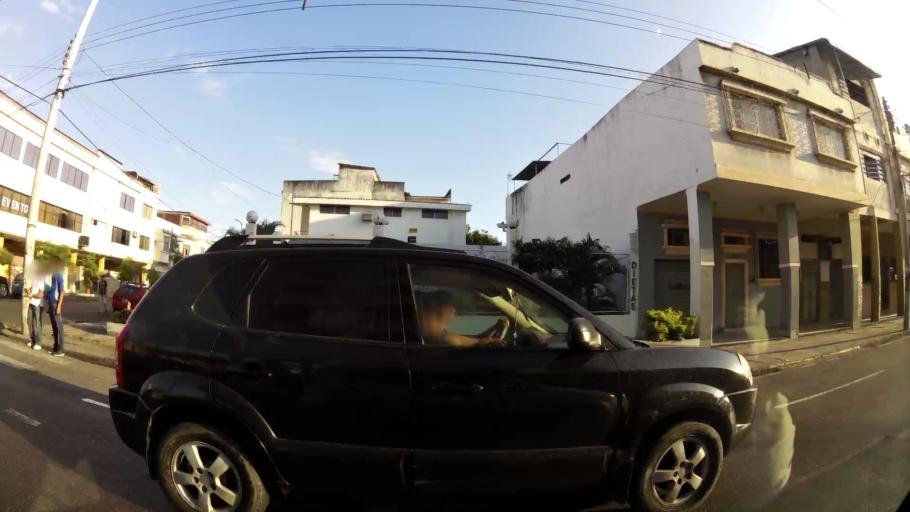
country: EC
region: Guayas
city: Guayaquil
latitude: -2.2090
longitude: -79.8903
